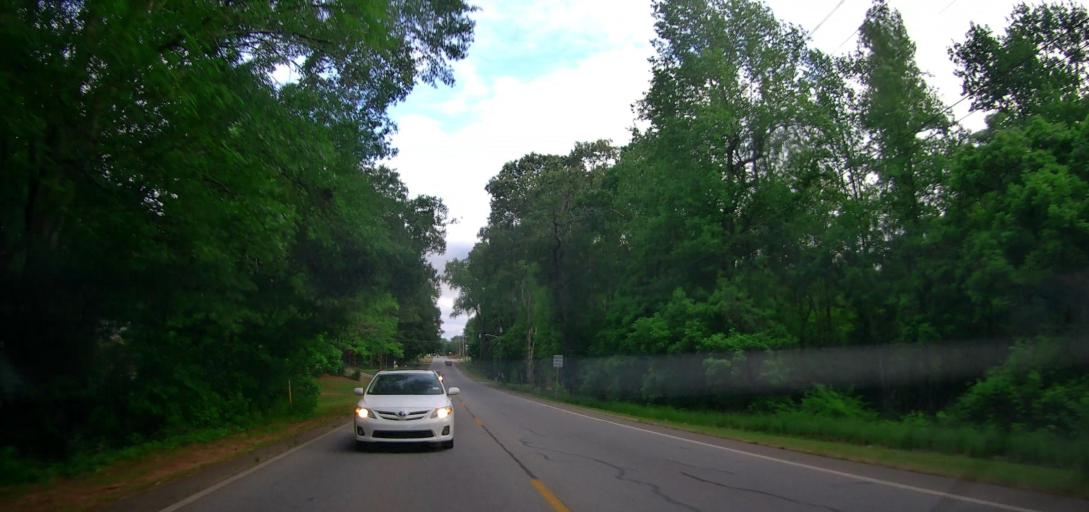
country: US
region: Georgia
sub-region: Oconee County
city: Watkinsville
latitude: 33.8717
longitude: -83.4121
